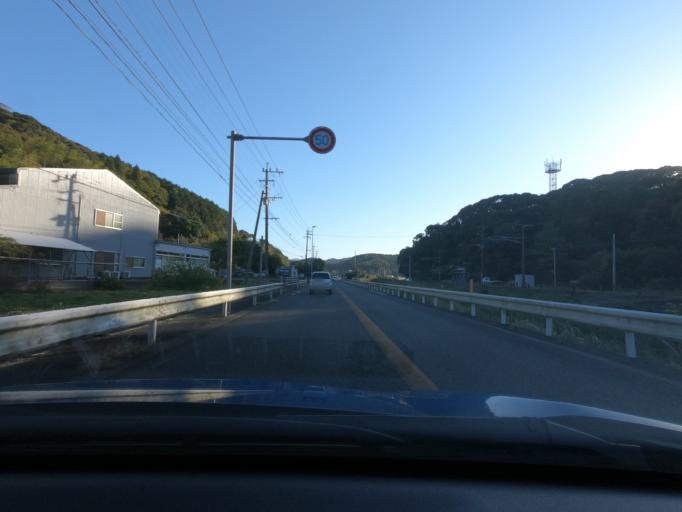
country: JP
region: Kagoshima
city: Satsumasendai
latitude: 31.8696
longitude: 130.2250
